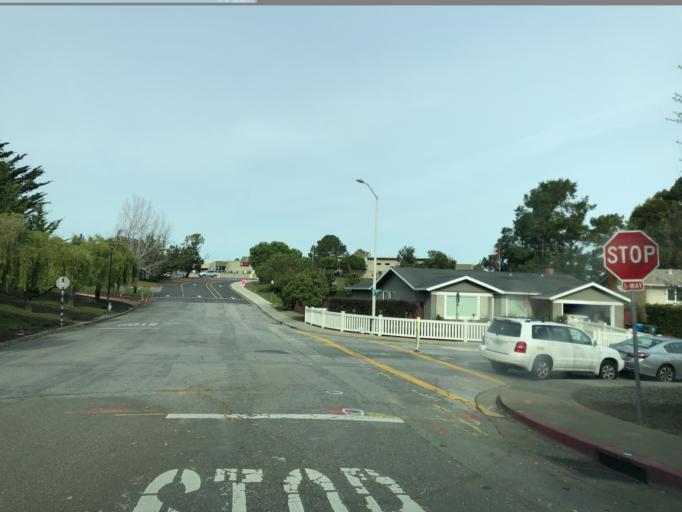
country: US
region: California
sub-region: San Mateo County
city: Highlands-Baywood Park
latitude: 37.5080
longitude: -122.3220
